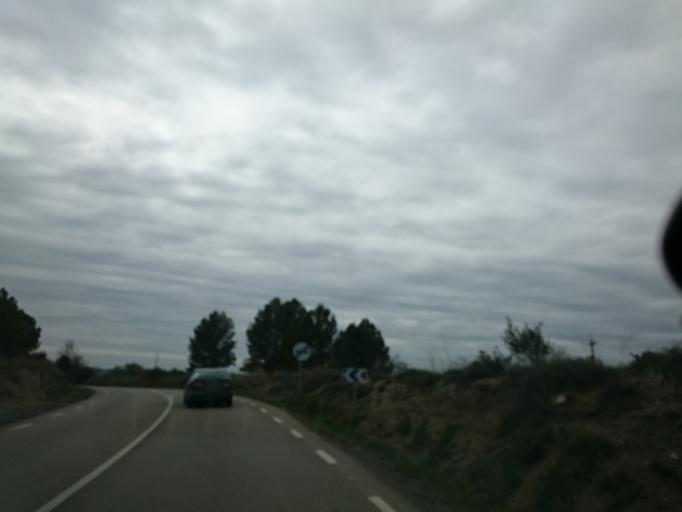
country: ES
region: Catalonia
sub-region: Provincia de Barcelona
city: Piera
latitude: 41.5220
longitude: 1.7420
